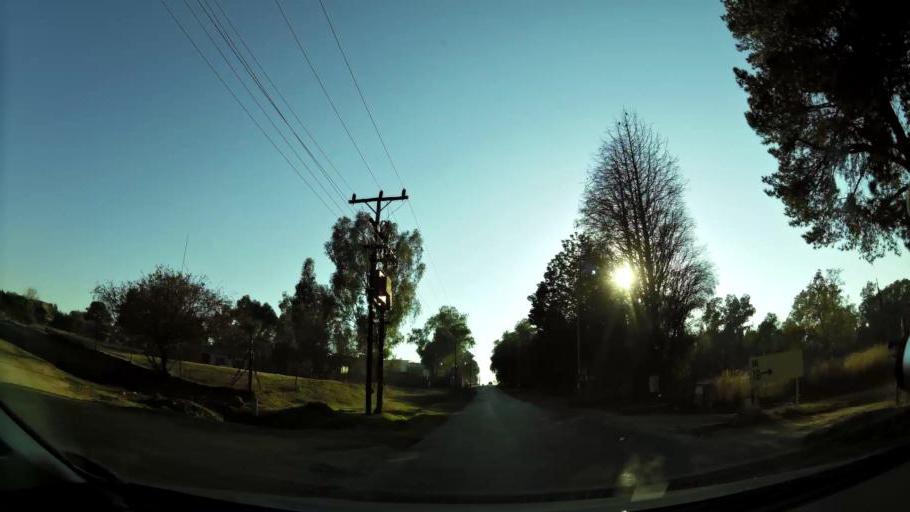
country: ZA
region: Gauteng
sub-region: City of Johannesburg Metropolitan Municipality
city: Midrand
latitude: -26.0241
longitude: 28.1308
